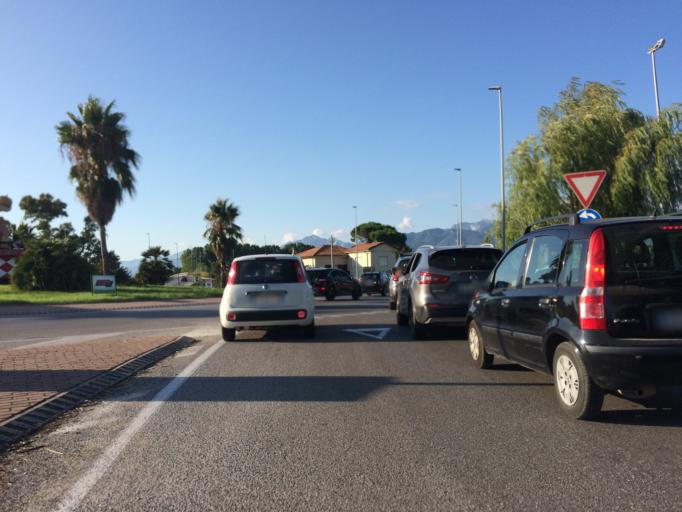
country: IT
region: Tuscany
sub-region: Provincia di Lucca
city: Camaiore
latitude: 43.8921
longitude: 10.2488
